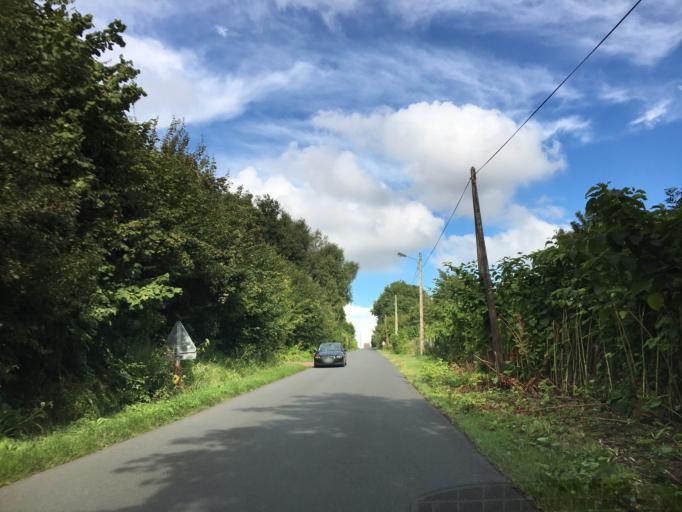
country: FR
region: Lower Normandy
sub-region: Departement du Calvados
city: Houlgate
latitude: 49.3014
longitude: -0.0623
